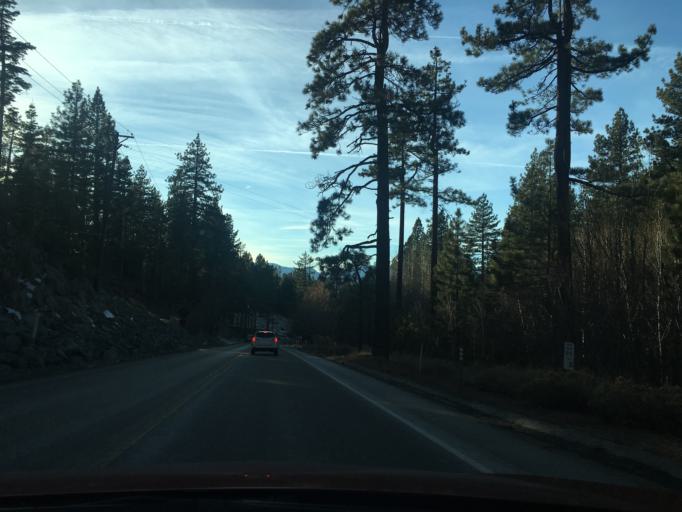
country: US
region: Nevada
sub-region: Douglas County
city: Kingsbury
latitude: 38.9673
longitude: -119.9186
